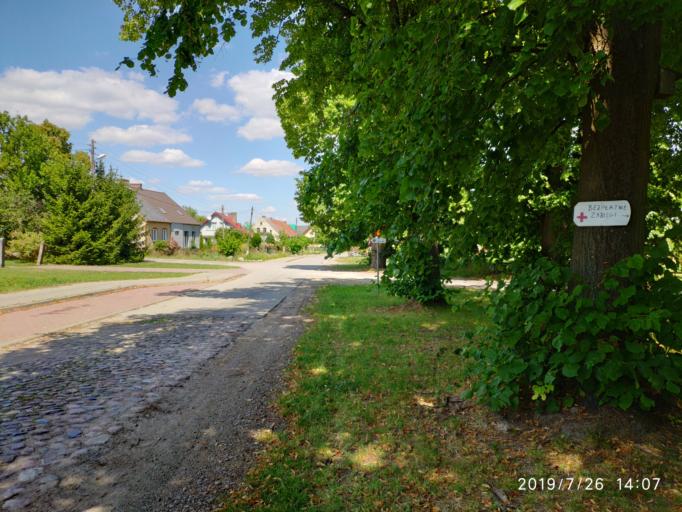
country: PL
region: Lubusz
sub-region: Powiat swiebodzinski
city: Lagow
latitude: 52.3554
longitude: 15.2712
